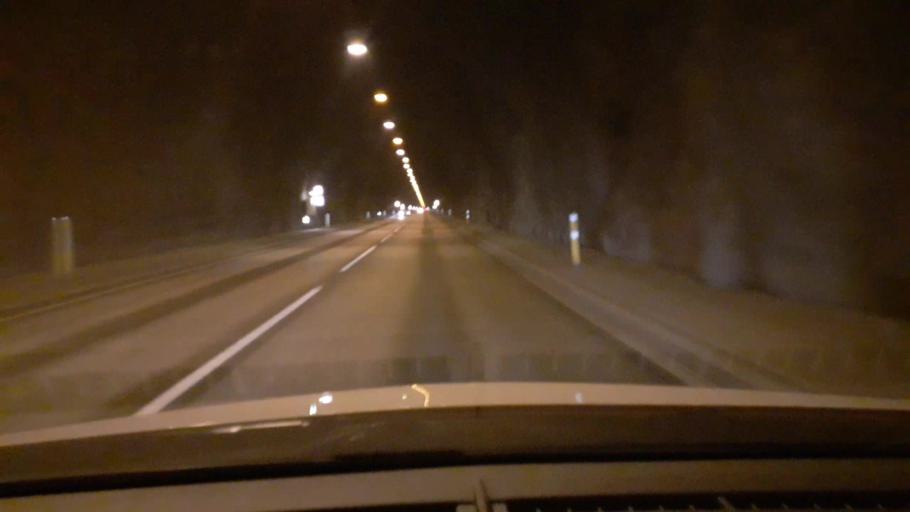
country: IS
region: Capital Region
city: Reykjavik
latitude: 64.2975
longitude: -21.8752
